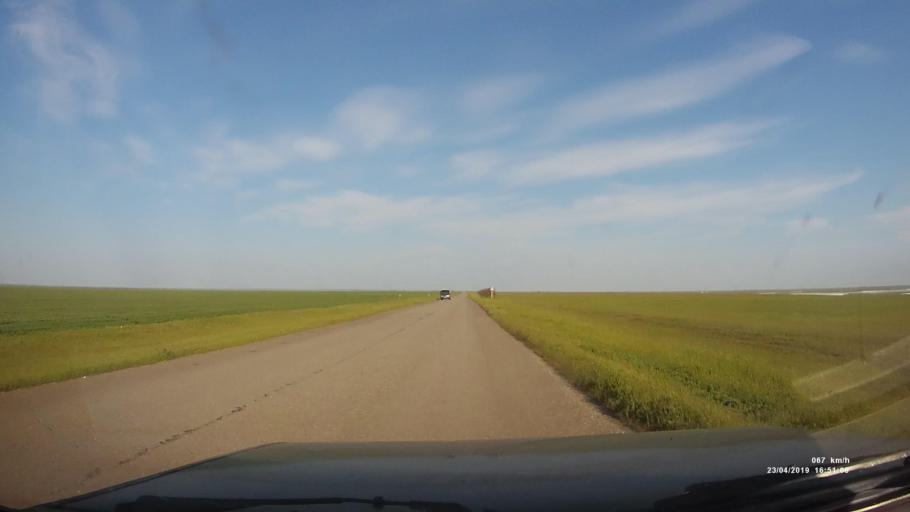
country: RU
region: Kalmykiya
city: Priyutnoye
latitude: 46.3243
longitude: 43.3016
